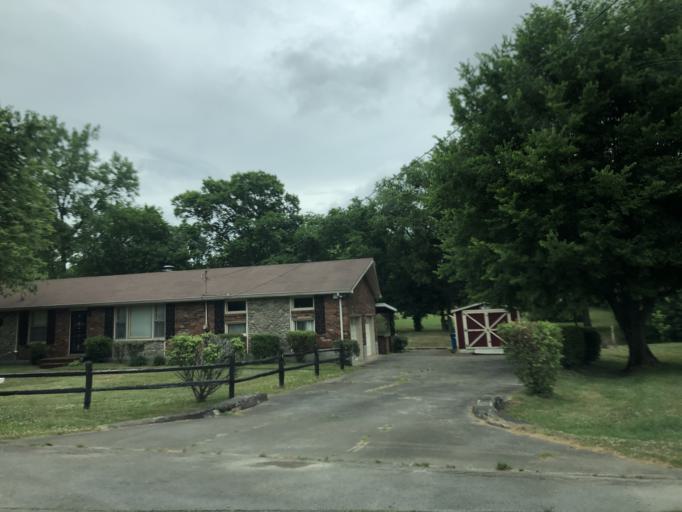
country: US
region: Tennessee
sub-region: Davidson County
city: Goodlettsville
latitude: 36.2704
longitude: -86.7652
